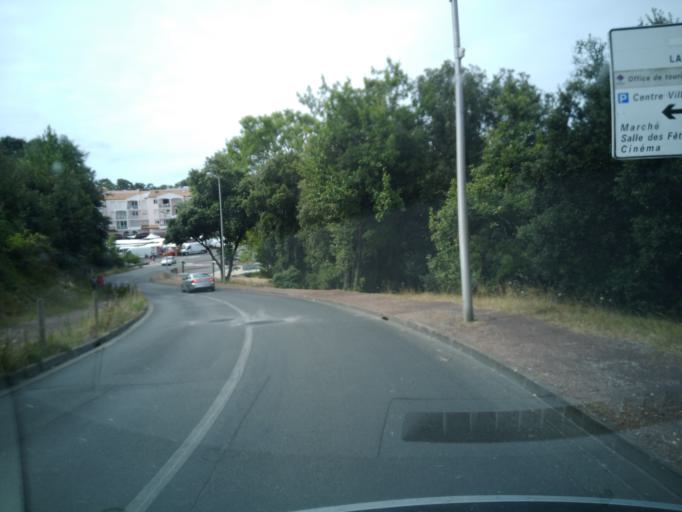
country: FR
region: Poitou-Charentes
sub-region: Departement de la Charente-Maritime
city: Saint-Palais-sur-Mer
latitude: 45.6465
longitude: -1.0894
